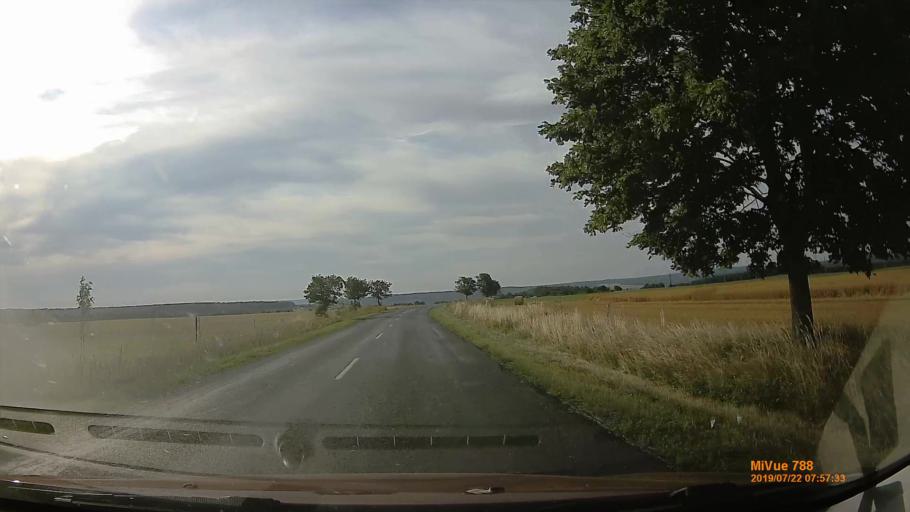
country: HU
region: Veszprem
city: Ajka
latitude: 47.0162
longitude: 17.5855
